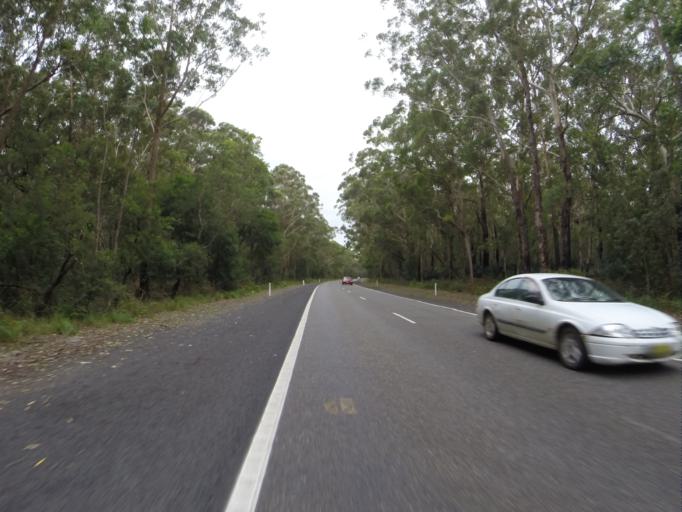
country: AU
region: New South Wales
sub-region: Shoalhaven Shire
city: Berry
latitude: -34.8164
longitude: 150.7476
